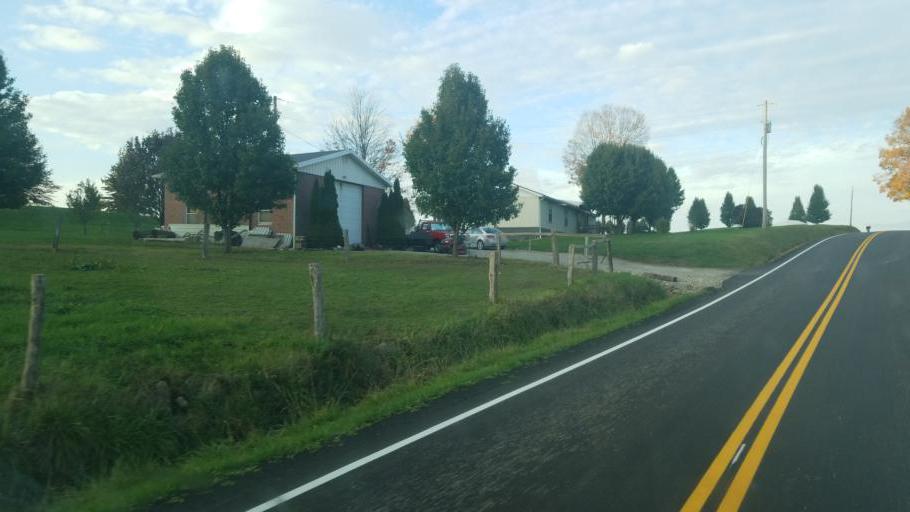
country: US
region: Ohio
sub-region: Wayne County
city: Shreve
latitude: 40.5851
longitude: -82.0669
